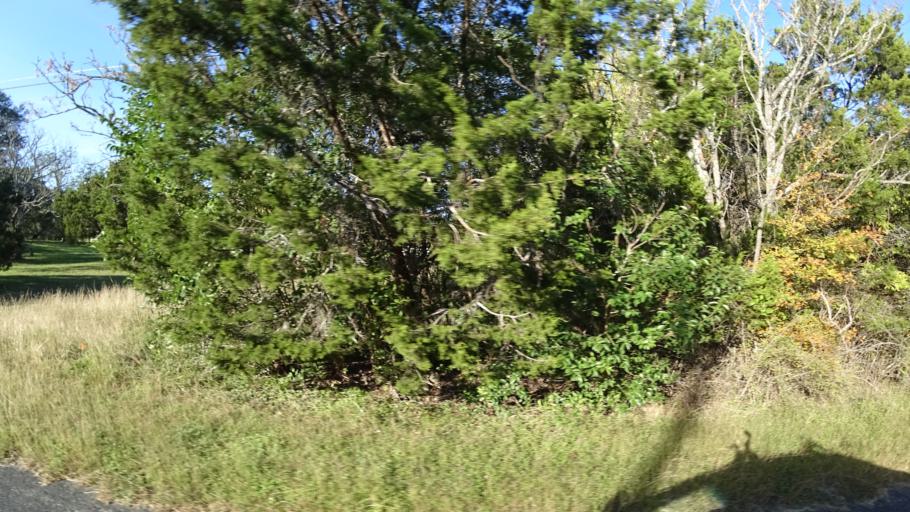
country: US
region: Texas
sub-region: Travis County
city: Barton Creek
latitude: 30.2422
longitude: -97.9107
